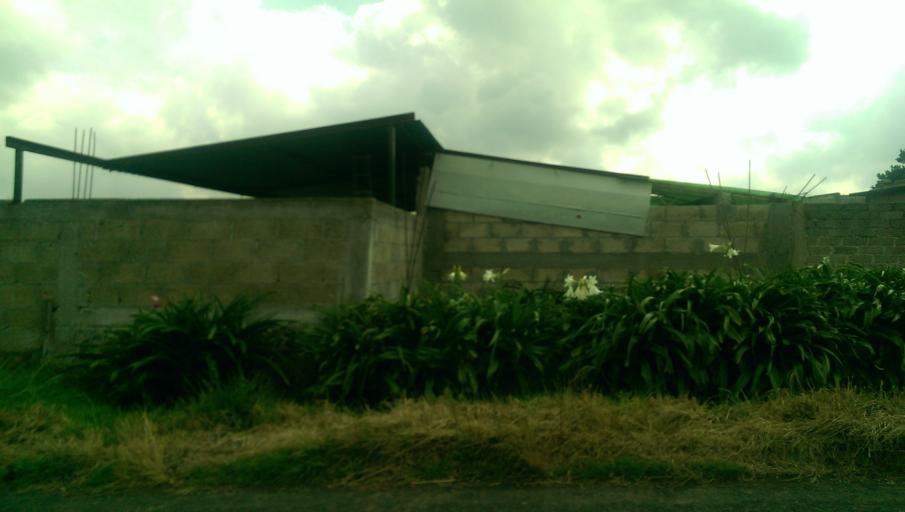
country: MX
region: Mexico
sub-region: Jilotepec
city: Jilotepec de Molina Enriquez
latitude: 19.9522
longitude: -99.4869
